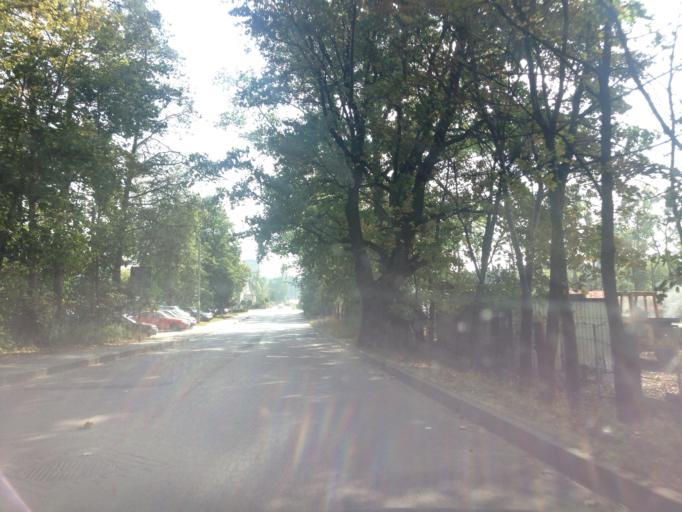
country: PL
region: Kujawsko-Pomorskie
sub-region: Powiat brodnicki
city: Brodnica
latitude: 53.2718
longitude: 19.4210
